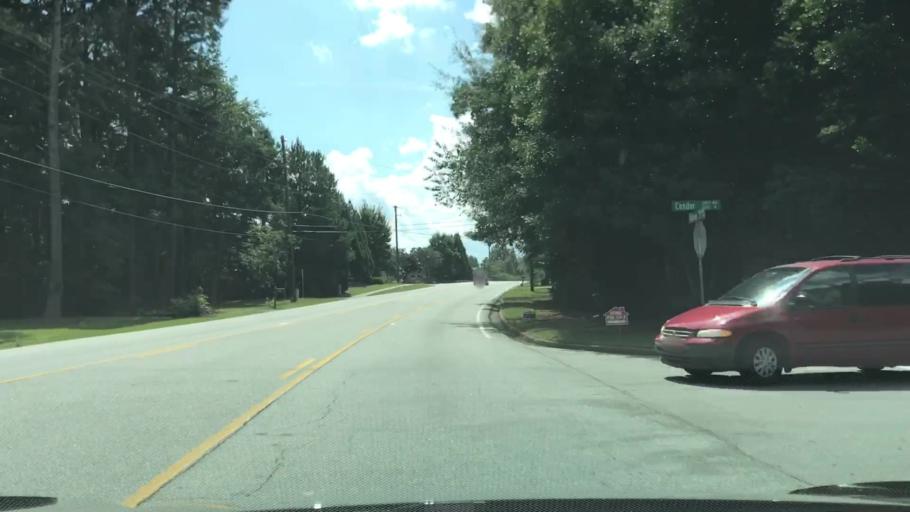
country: US
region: Georgia
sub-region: Gwinnett County
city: Lawrenceville
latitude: 33.9409
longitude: -84.0595
